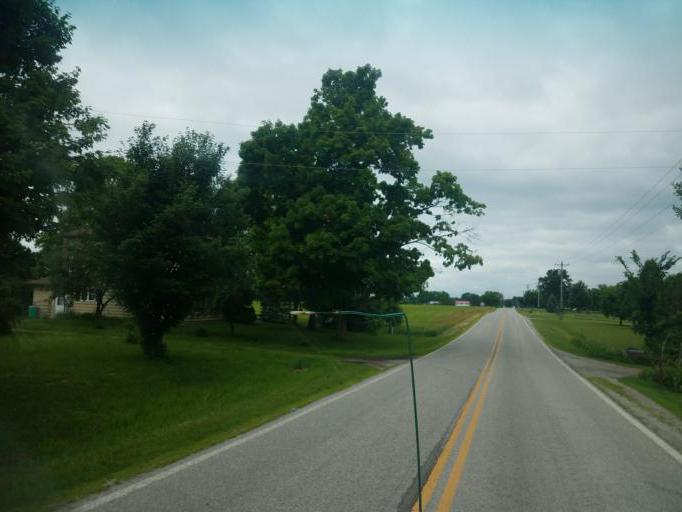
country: US
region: Ohio
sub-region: Champaign County
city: North Lewisburg
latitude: 40.4113
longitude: -83.4994
